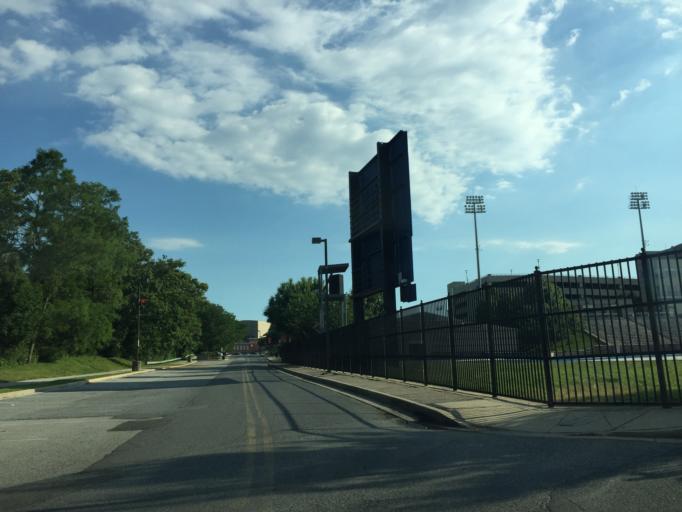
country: US
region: Maryland
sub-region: Baltimore County
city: Parkville
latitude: 39.3441
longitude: -76.5817
